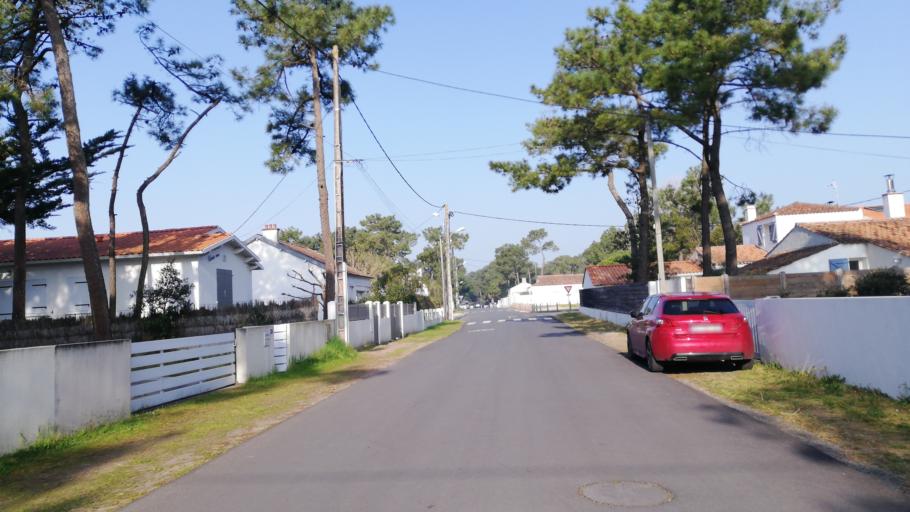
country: FR
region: Pays de la Loire
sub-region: Departement de la Vendee
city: La Tranche-sur-Mer
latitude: 46.3474
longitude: -1.4164
